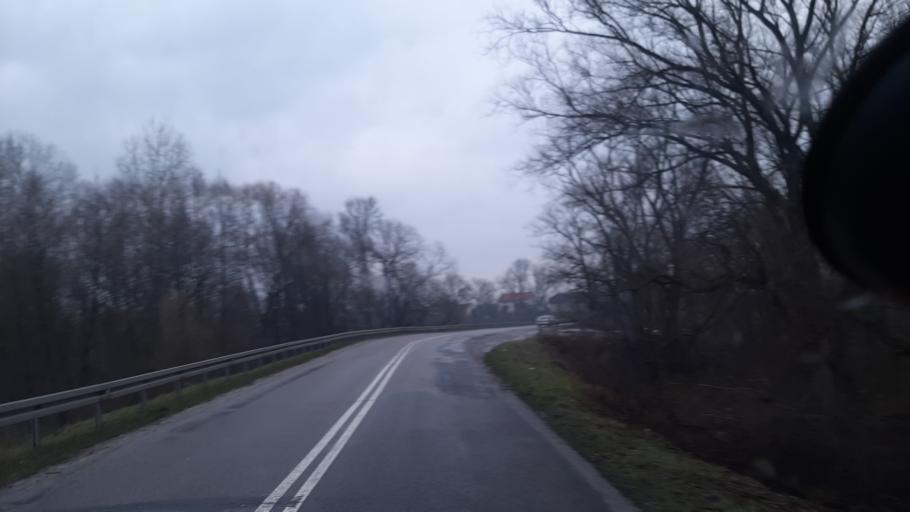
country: PL
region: Lublin Voivodeship
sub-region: Powiat lubartowski
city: Serniki
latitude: 51.4349
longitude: 22.6543
